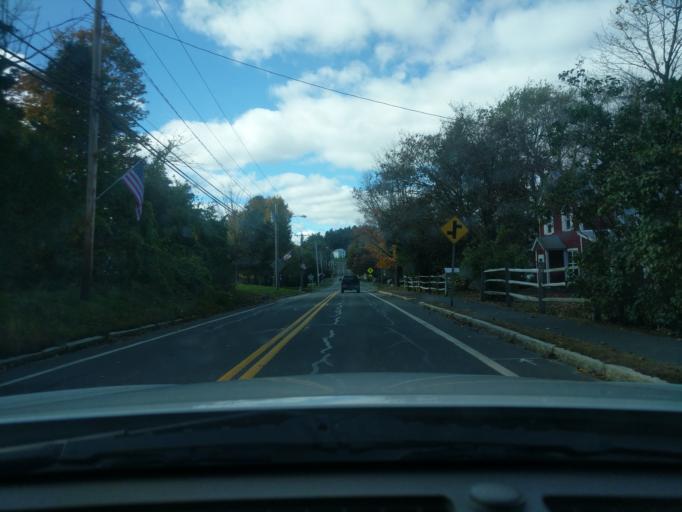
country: US
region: Massachusetts
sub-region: Hampden County
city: Granville
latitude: 42.1791
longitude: -72.9231
